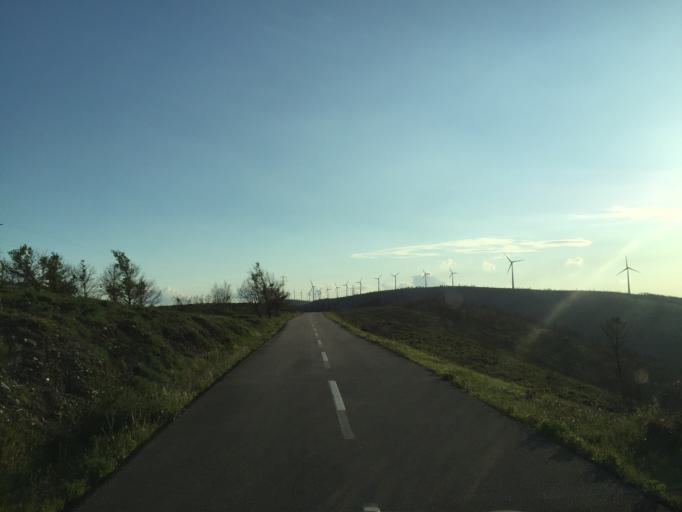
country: PT
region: Coimbra
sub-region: Pampilhosa da Serra
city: Pampilhosa da Serra
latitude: 40.1127
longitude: -8.0162
